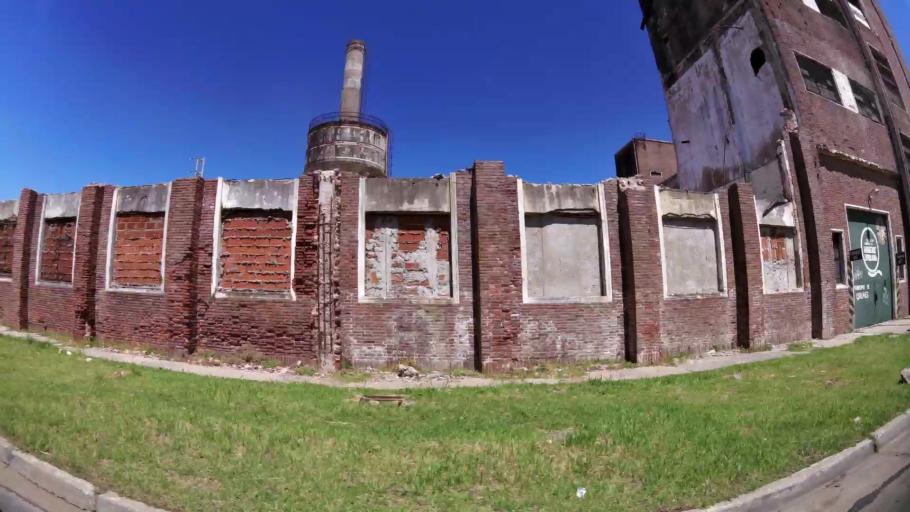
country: AR
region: Buenos Aires
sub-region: Partido de Quilmes
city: Quilmes
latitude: -34.7216
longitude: -58.2829
